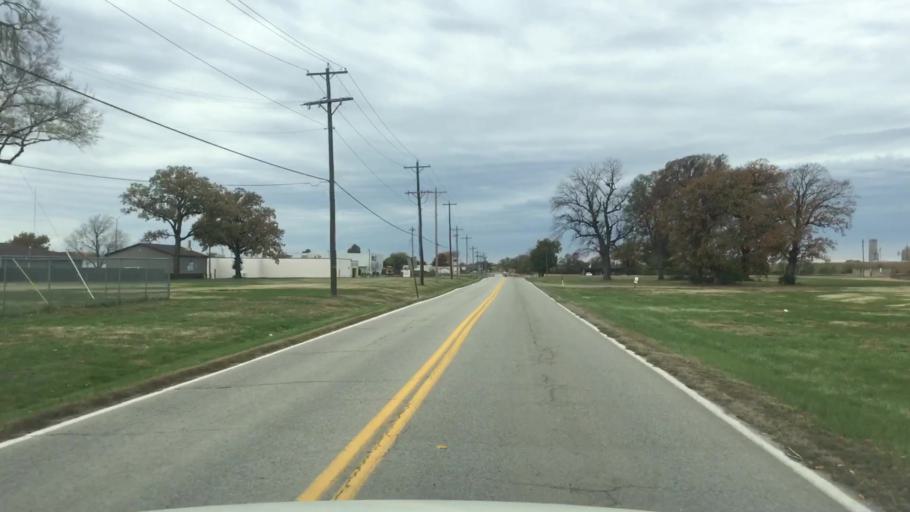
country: US
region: Kansas
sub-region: Shawnee County
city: Topeka
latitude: 39.0815
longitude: -95.7202
